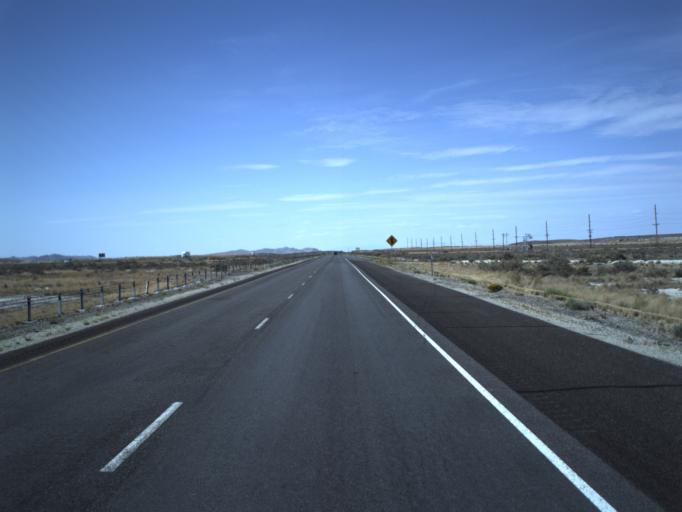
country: US
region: Utah
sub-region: Tooele County
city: Grantsville
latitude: 40.7315
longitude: -113.1173
